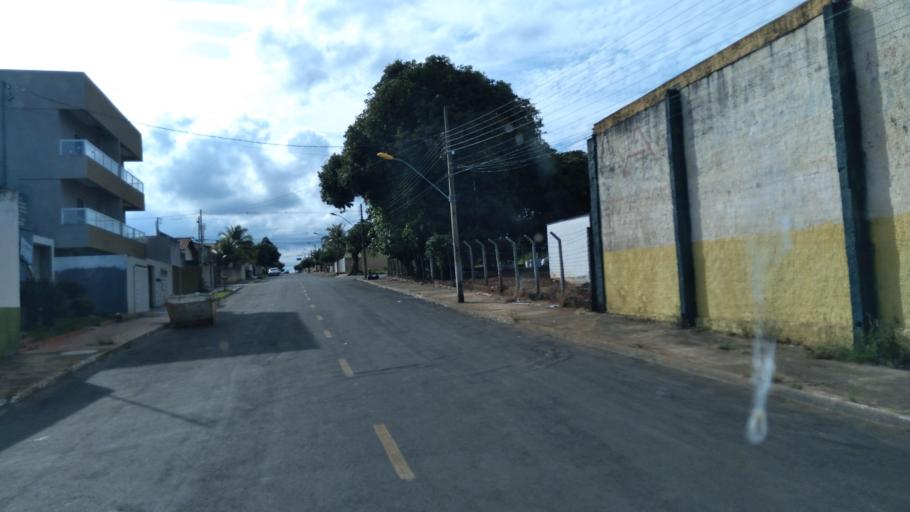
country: BR
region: Goias
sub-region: Mineiros
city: Mineiros
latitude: -17.5657
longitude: -52.5628
